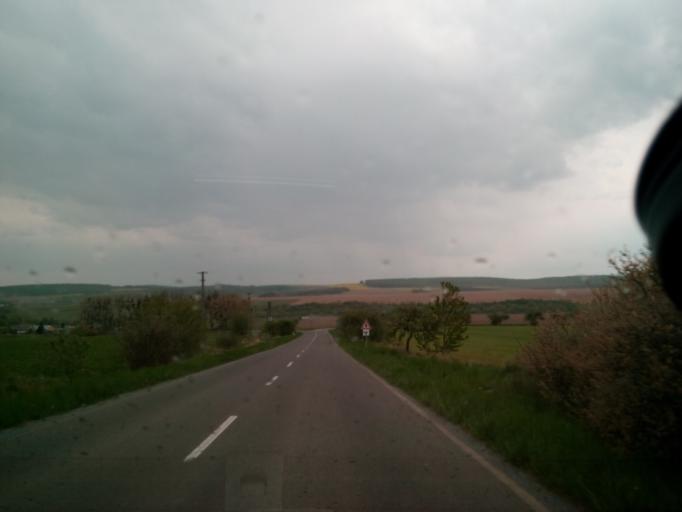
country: SK
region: Kosicky
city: Kosice
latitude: 48.7464
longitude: 21.4428
